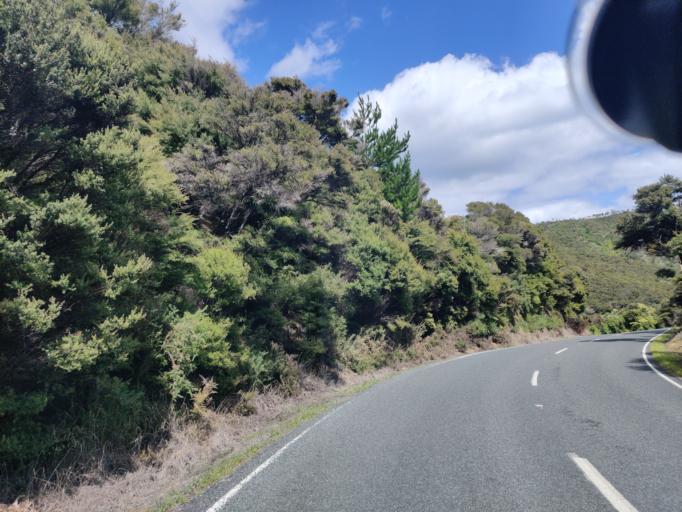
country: NZ
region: Northland
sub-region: Far North District
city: Paihia
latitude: -35.2597
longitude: 174.2277
